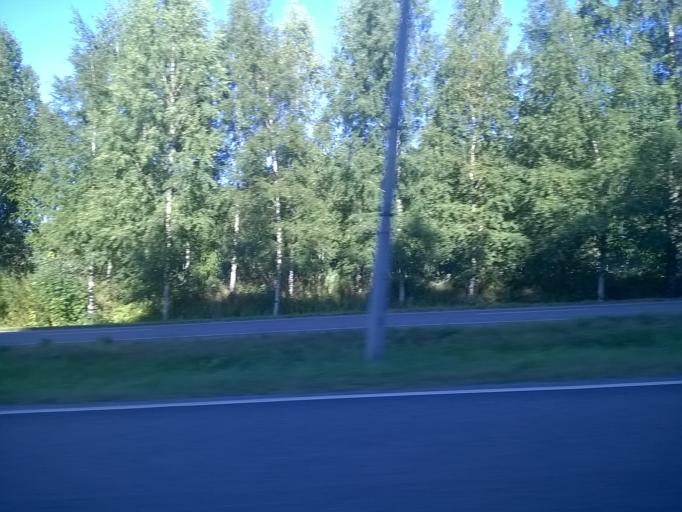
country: FI
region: Pirkanmaa
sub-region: Tampere
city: Tampere
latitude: 61.4671
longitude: 23.8415
